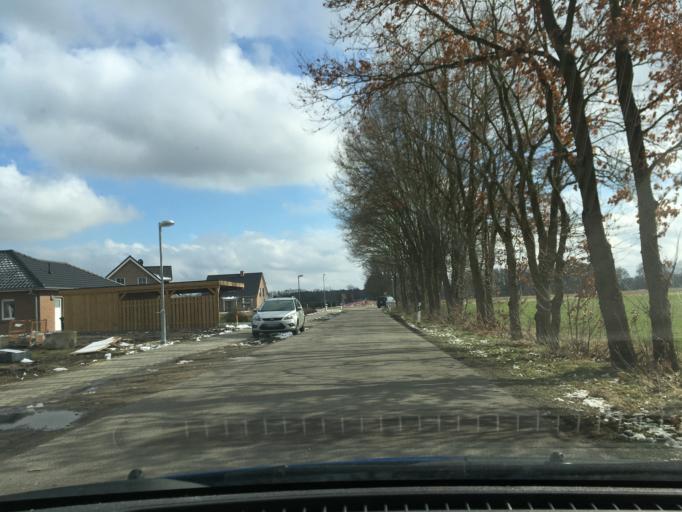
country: DE
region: Lower Saxony
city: Handorf
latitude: 53.3338
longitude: 10.3515
